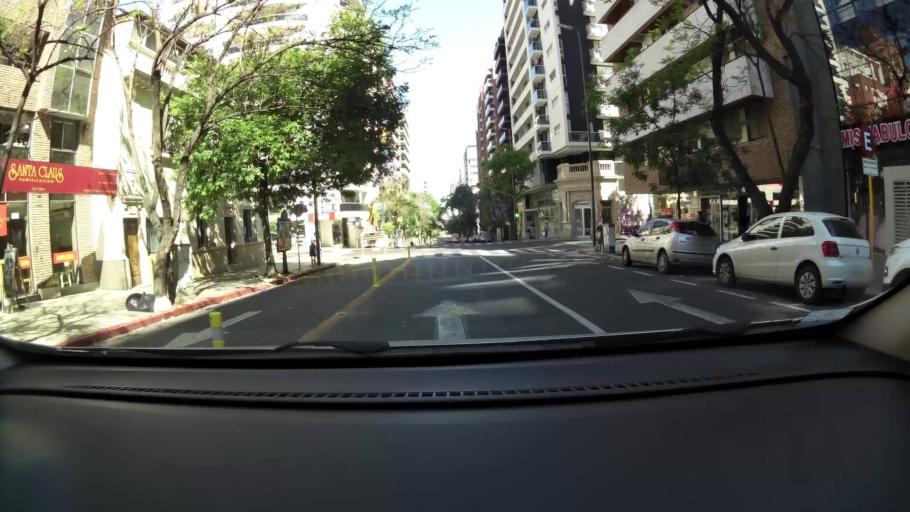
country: AR
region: Cordoba
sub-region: Departamento de Capital
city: Cordoba
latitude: -31.4269
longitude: -64.1898
